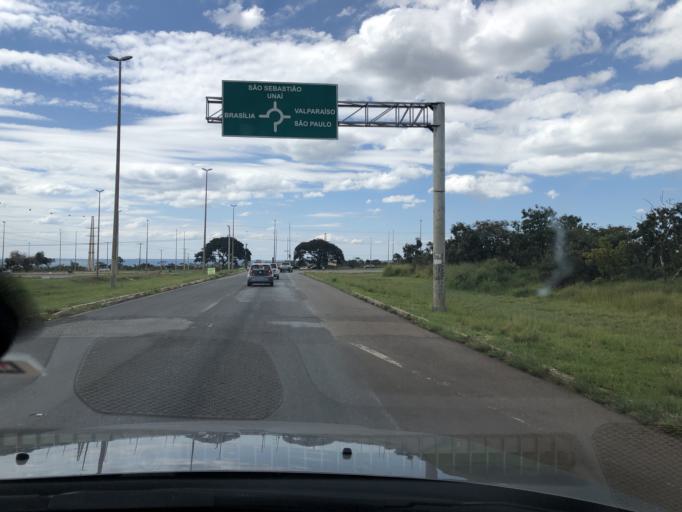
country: BR
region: Federal District
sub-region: Brasilia
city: Brasilia
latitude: -15.9772
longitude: -47.9919
